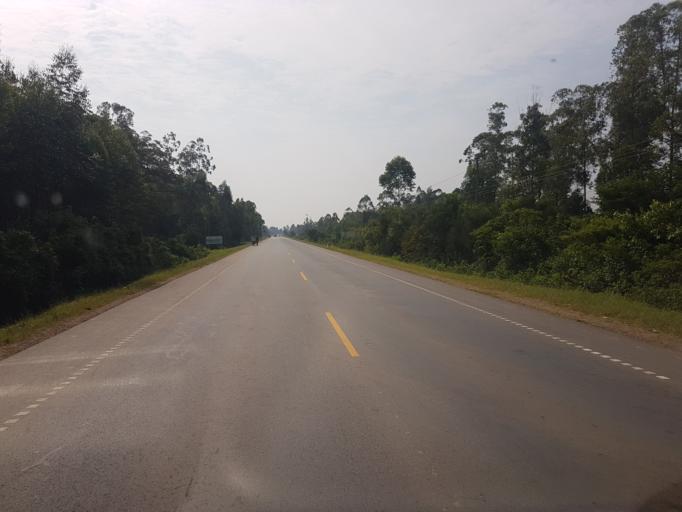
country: UG
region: Western Region
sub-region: Sheema District
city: Kibingo
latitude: -0.6350
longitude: 30.5267
